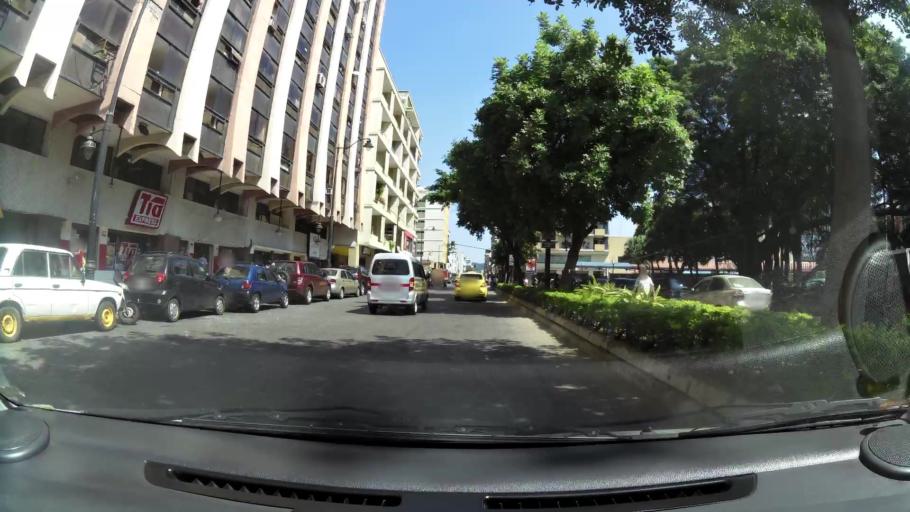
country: EC
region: Guayas
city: Guayaquil
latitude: -2.1910
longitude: -79.8881
